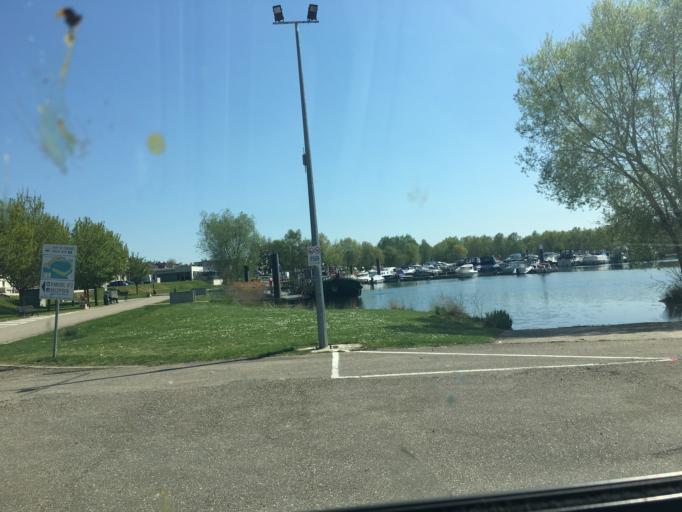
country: FR
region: Lorraine
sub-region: Departement de Meurthe-et-Moselle
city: Pont-a-Mousson
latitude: 48.9023
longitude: 6.0614
